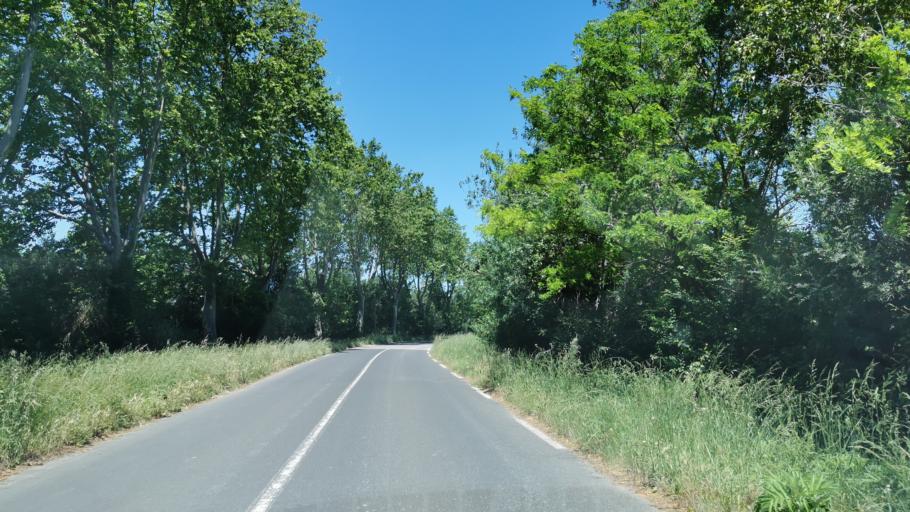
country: FR
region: Languedoc-Roussillon
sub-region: Departement de l'Aude
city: Canet
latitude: 43.2410
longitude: 2.8556
